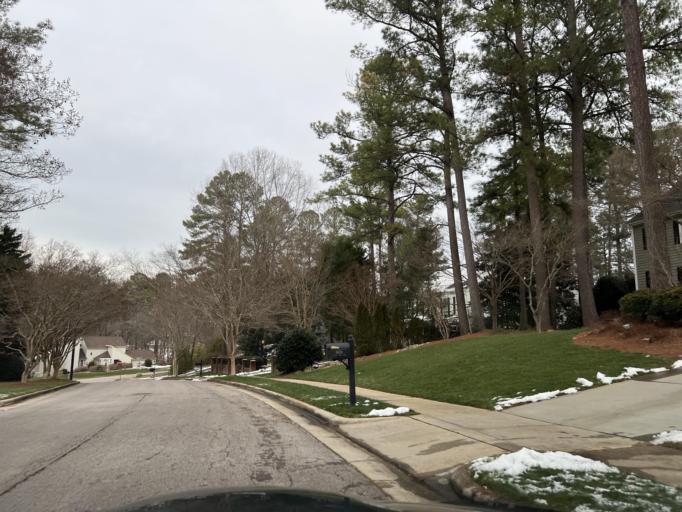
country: US
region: North Carolina
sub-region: Wake County
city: West Raleigh
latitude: 35.8739
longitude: -78.6043
